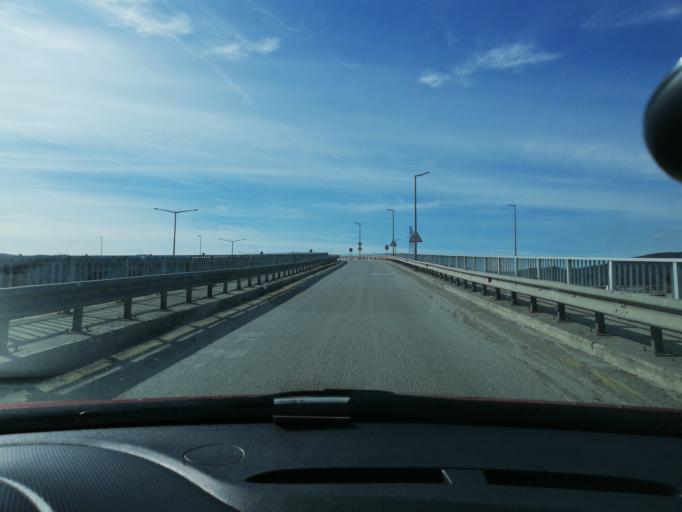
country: TR
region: Bolu
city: Bolu
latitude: 40.7251
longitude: 31.4639
